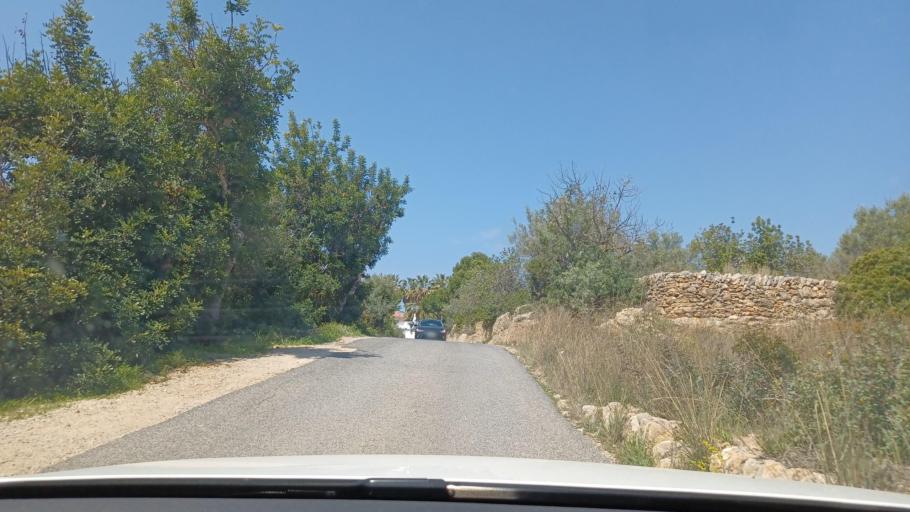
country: ES
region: Catalonia
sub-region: Provincia de Tarragona
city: L'Ampolla
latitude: 40.8283
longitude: 0.7399
